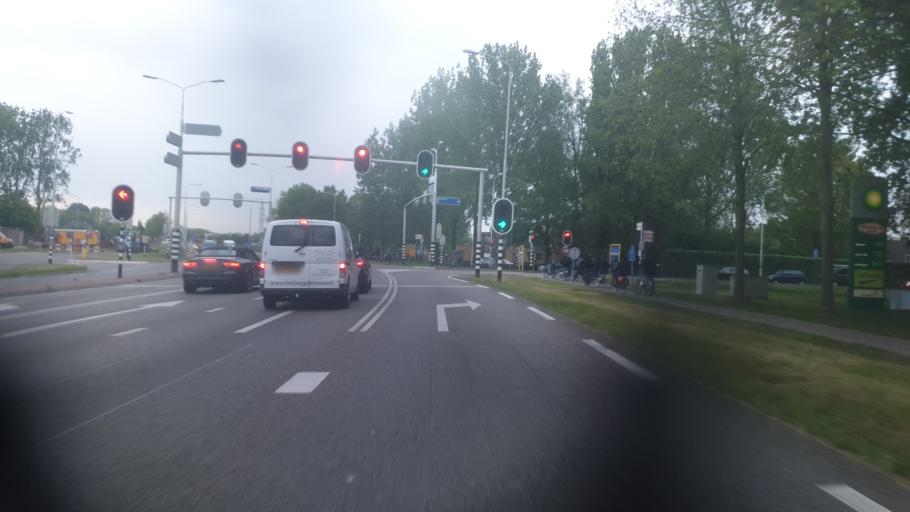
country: NL
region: Gelderland
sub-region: Gemeente Overbetuwe
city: Elst
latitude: 51.8958
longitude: 5.9120
